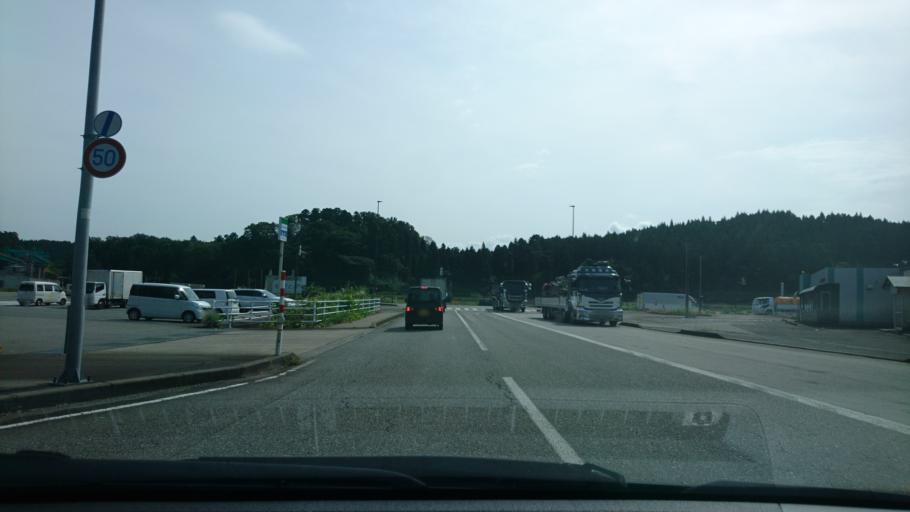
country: JP
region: Fukui
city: Maruoka
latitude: 36.2898
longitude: 136.2956
